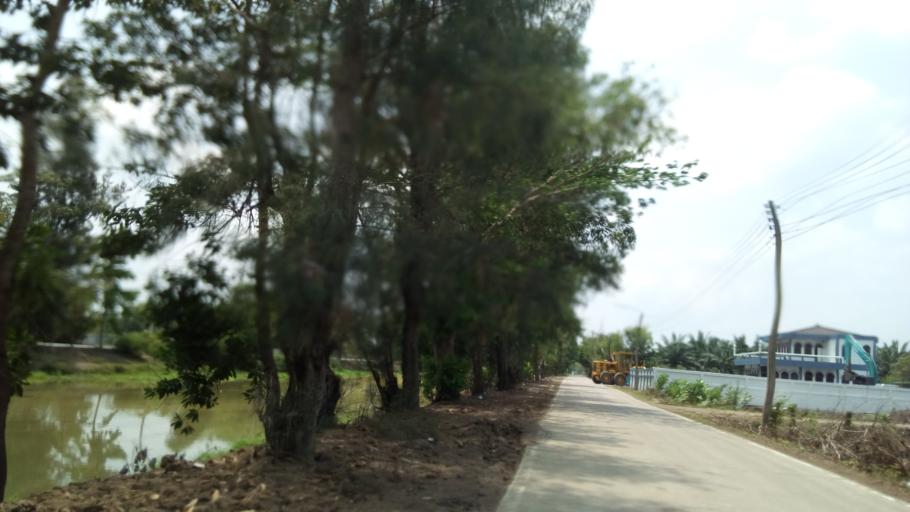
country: TH
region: Pathum Thani
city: Nong Suea
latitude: 14.1543
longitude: 100.8232
